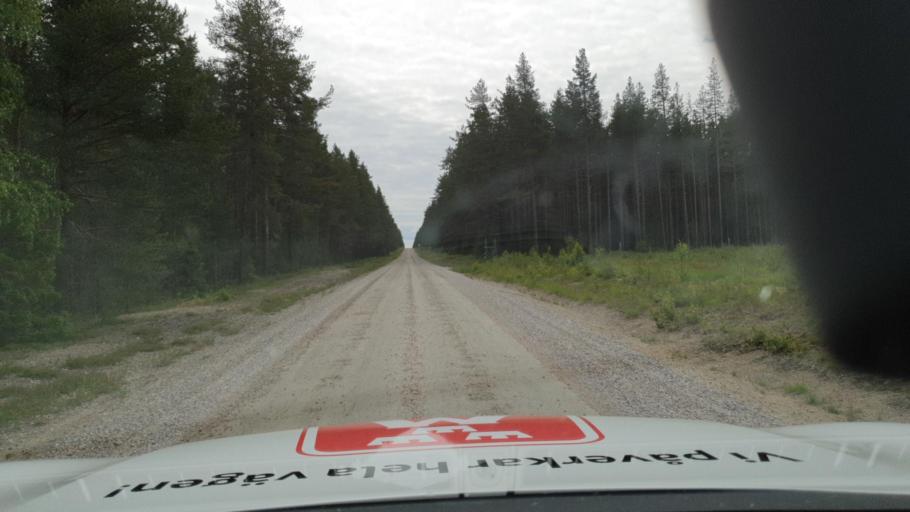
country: SE
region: Vaesterbotten
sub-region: Skelleftea Kommun
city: Forsbacka
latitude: 64.6526
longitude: 20.4431
